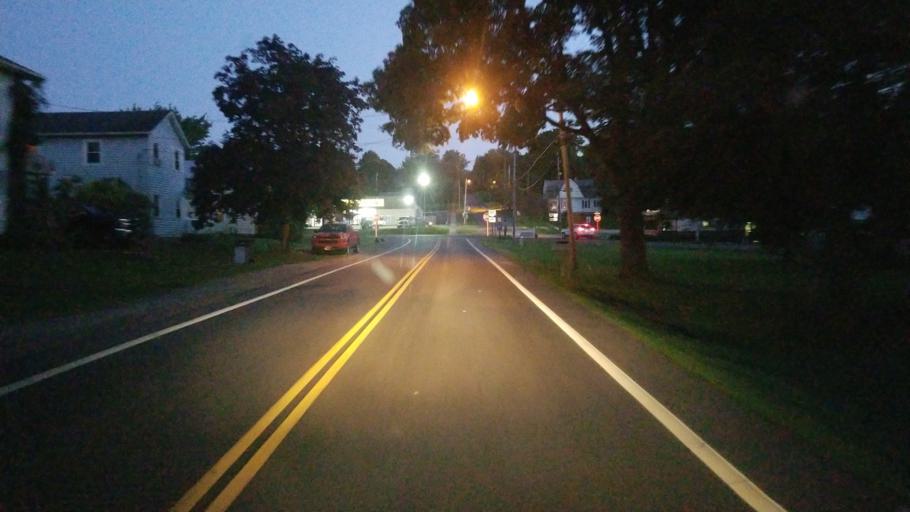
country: US
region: Ohio
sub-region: Sandusky County
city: Bellville
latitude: 40.5883
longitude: -82.4238
